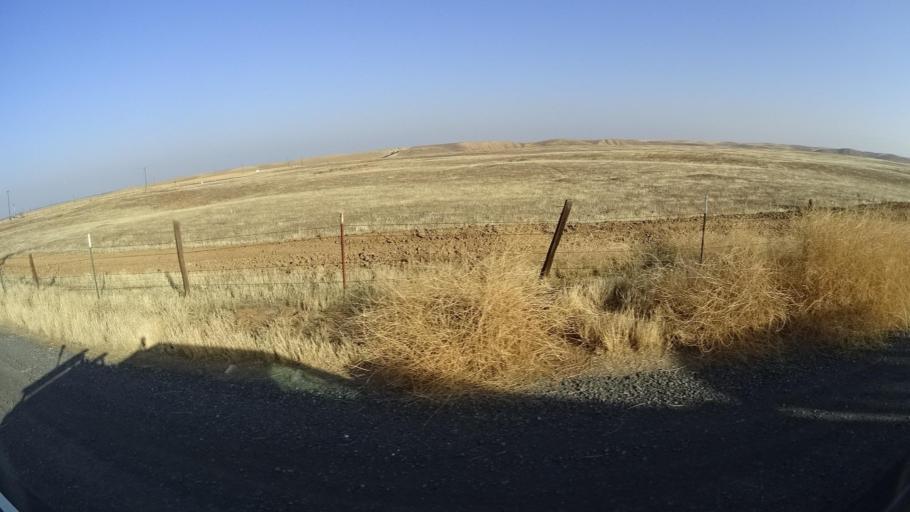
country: US
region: California
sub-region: Tulare County
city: Richgrove
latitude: 35.7625
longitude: -119.0518
